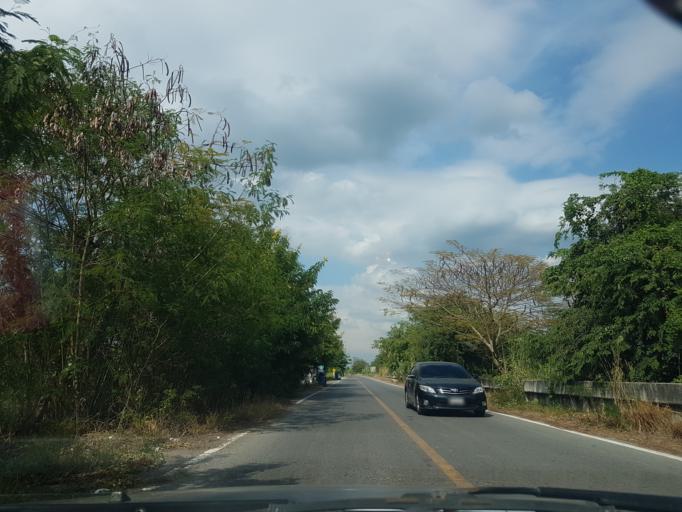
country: TH
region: Pathum Thani
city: Nong Suea
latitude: 14.1520
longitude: 100.8914
